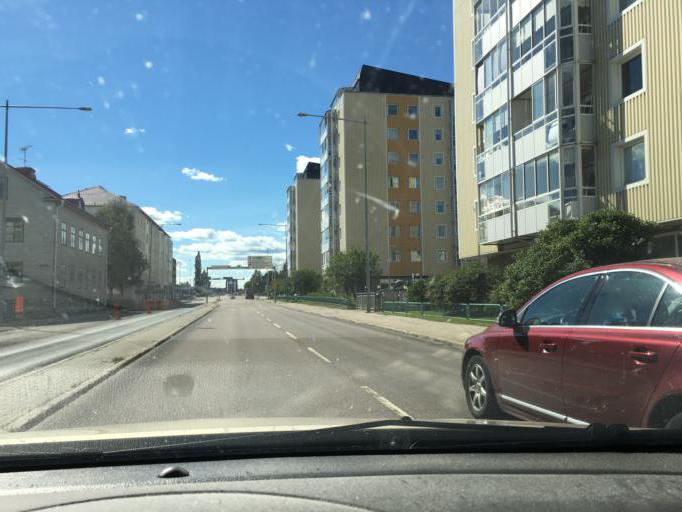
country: SE
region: Norrbotten
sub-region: Lulea Kommun
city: Lulea
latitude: 65.5809
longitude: 22.1414
